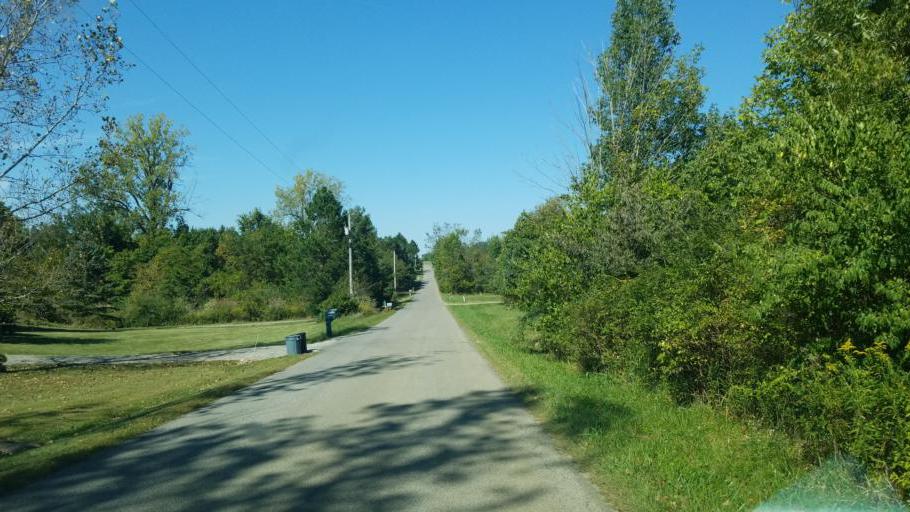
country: US
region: Ohio
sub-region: Logan County
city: Bellefontaine
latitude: 40.3107
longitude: -83.7160
